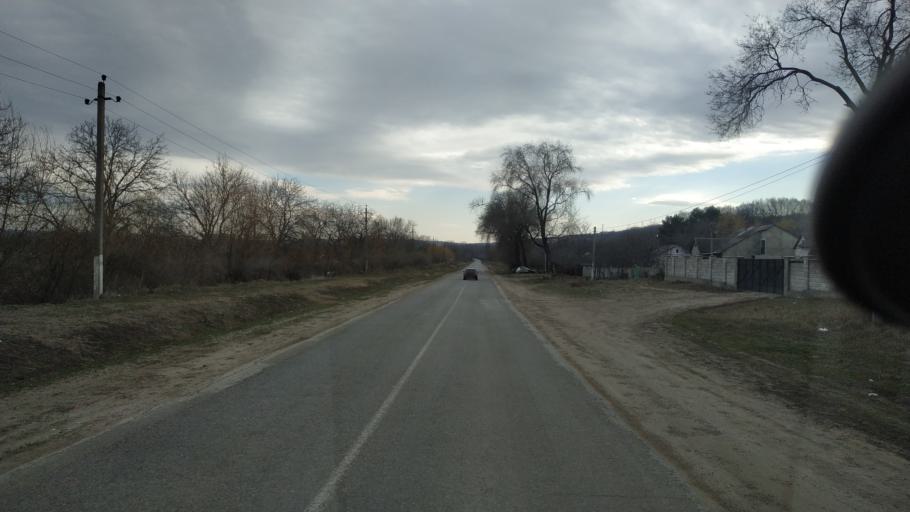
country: MD
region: Chisinau
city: Vadul lui Voda
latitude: 47.1375
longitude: 29.0610
